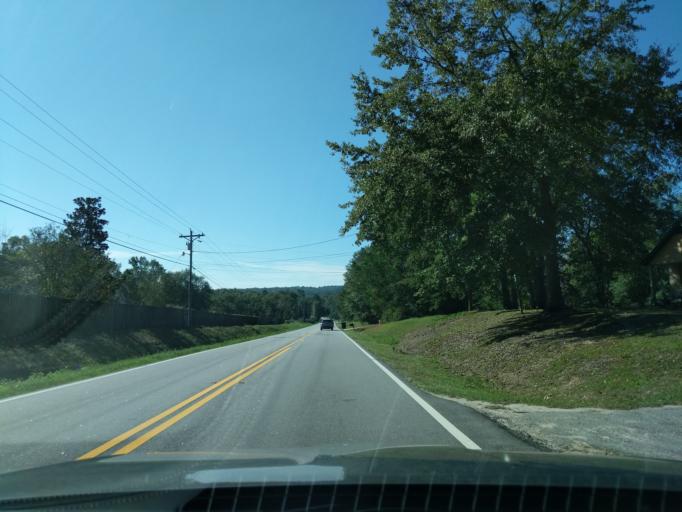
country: US
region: Georgia
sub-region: Richmond County
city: Hephzibah
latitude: 33.3499
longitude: -82.0018
